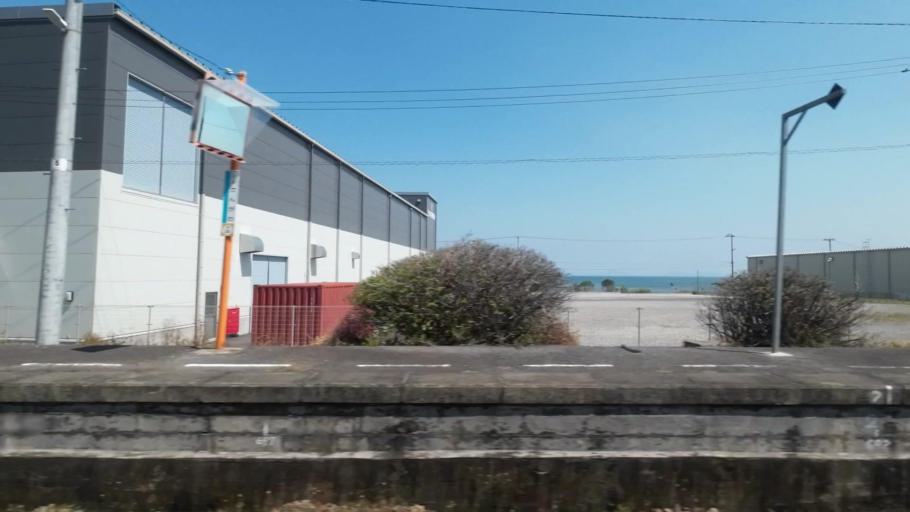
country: JP
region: Ehime
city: Kawanoecho
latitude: 33.9679
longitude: 133.4998
